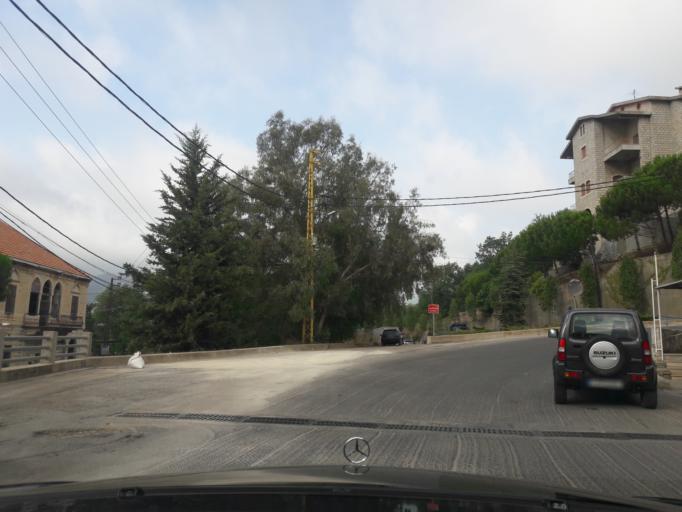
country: LB
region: Mont-Liban
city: Djounie
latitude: 33.9265
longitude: 35.7374
